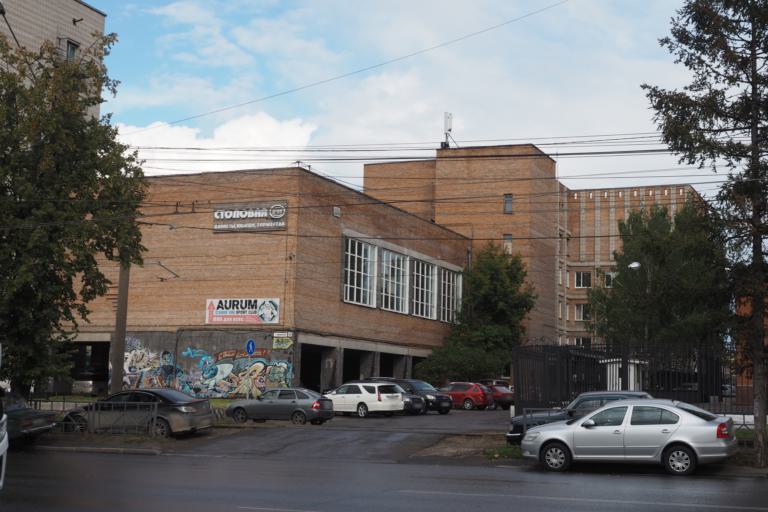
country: RU
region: Tomsk
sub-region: Tomskiy Rayon
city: Tomsk
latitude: 56.4677
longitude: 84.9813
